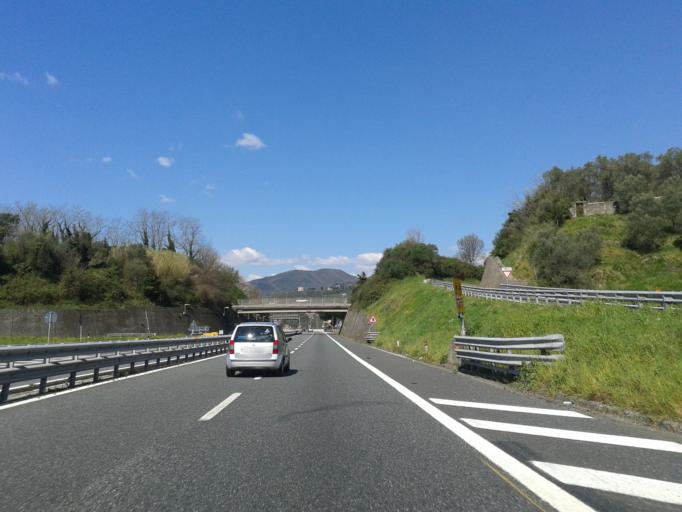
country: IT
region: Liguria
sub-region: Provincia di Genova
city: Lavagna
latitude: 44.3171
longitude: 9.3516
